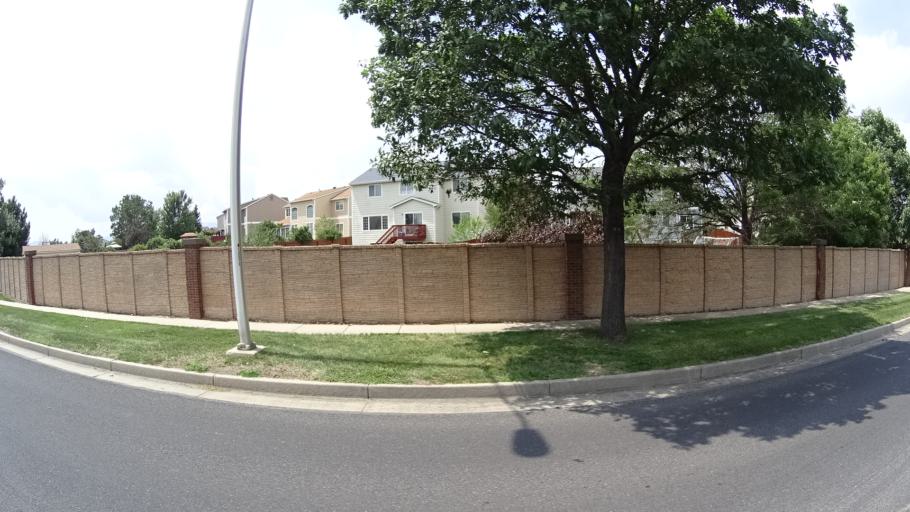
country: US
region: Colorado
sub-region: El Paso County
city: Cimarron Hills
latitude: 38.9141
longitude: -104.7337
